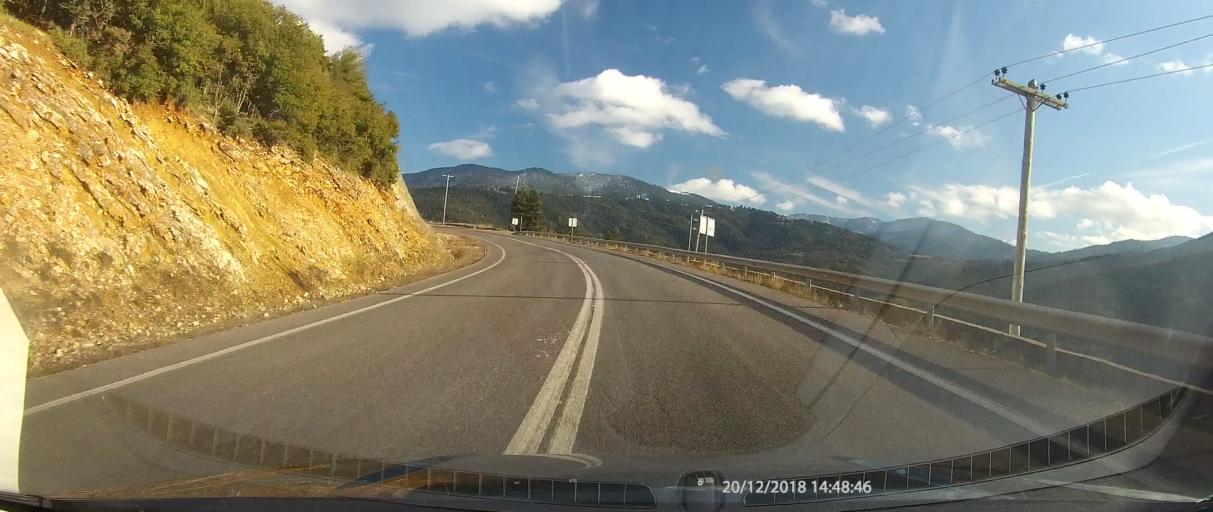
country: GR
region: Central Greece
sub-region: Nomos Evrytanias
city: Karpenisi
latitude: 38.9023
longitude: 21.7940
